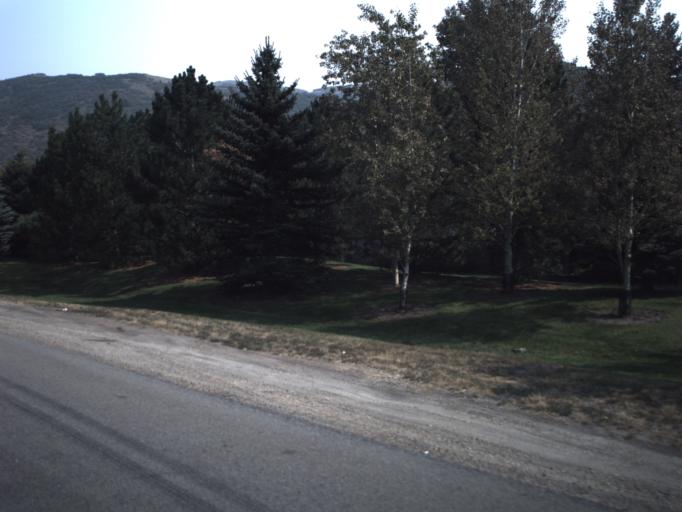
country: US
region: Utah
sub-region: Summit County
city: Park City
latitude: 40.6682
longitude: -111.4880
